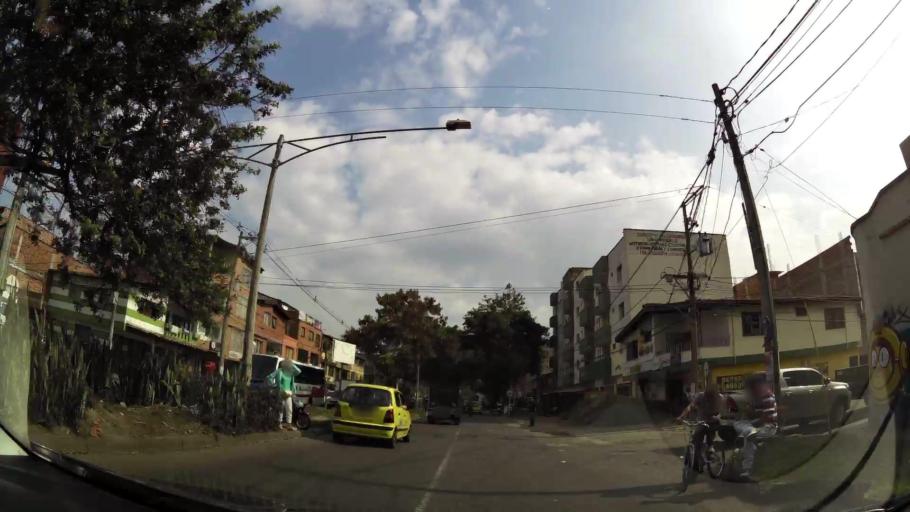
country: CO
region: Antioquia
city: Medellin
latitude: 6.2280
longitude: -75.5832
